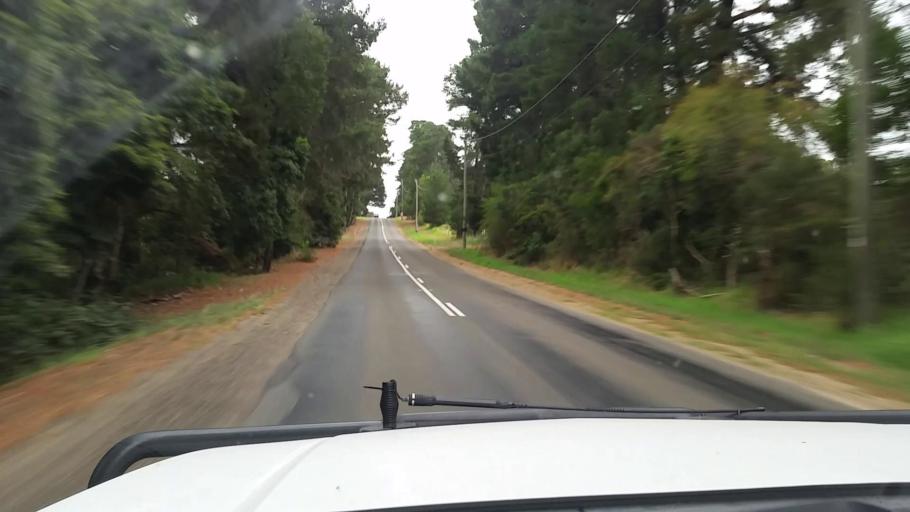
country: AU
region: Victoria
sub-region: Mornington Peninsula
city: Hastings
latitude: -38.3076
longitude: 145.1456
